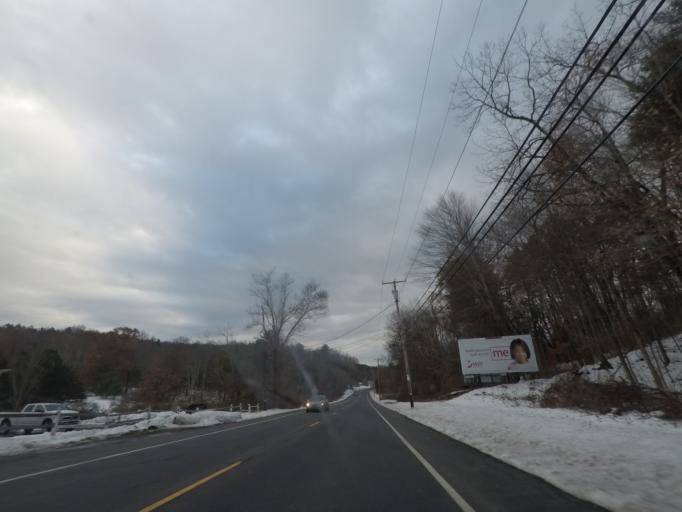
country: US
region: New York
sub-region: Ulster County
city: Kingston
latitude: 41.9030
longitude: -74.0279
